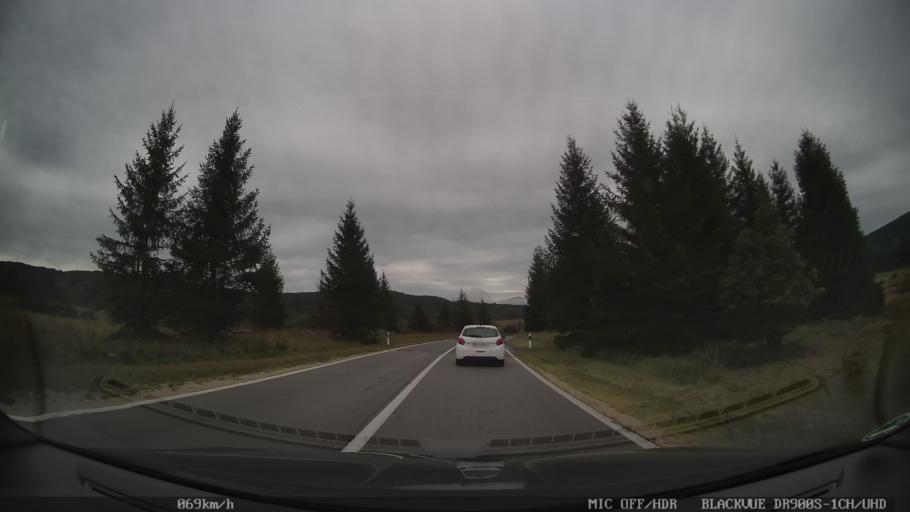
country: HR
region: Licko-Senjska
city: Jezerce
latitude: 44.7976
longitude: 15.5721
